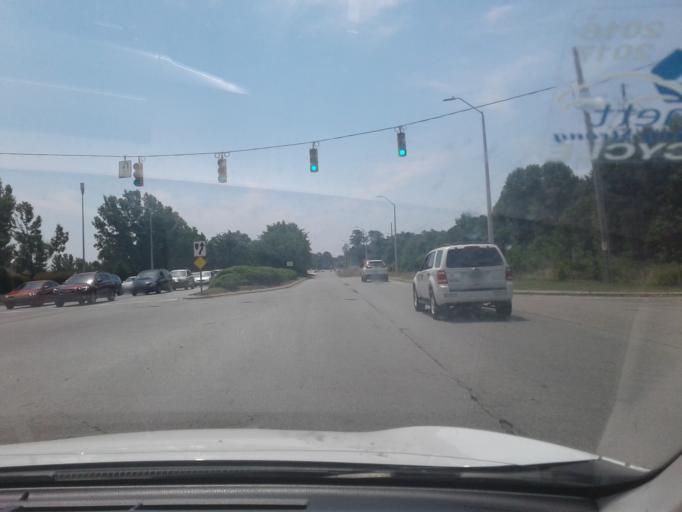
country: US
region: North Carolina
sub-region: Wake County
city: Garner
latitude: 35.6927
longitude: -78.5838
